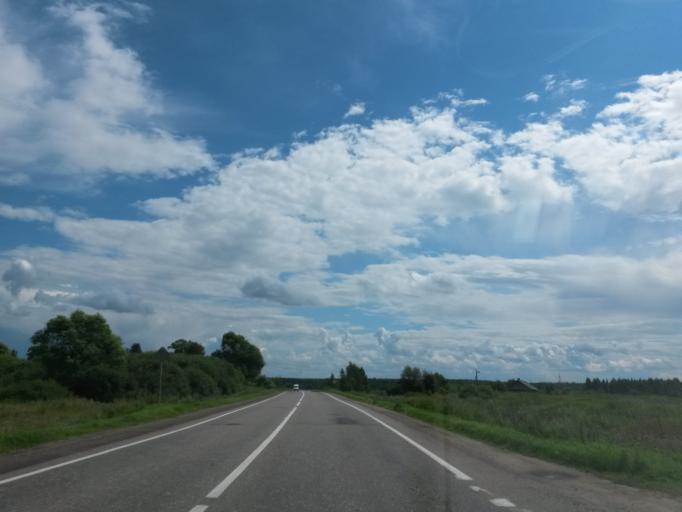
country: RU
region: Jaroslavl
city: Gavrilov-Yam
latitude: 57.3060
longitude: 39.9404
